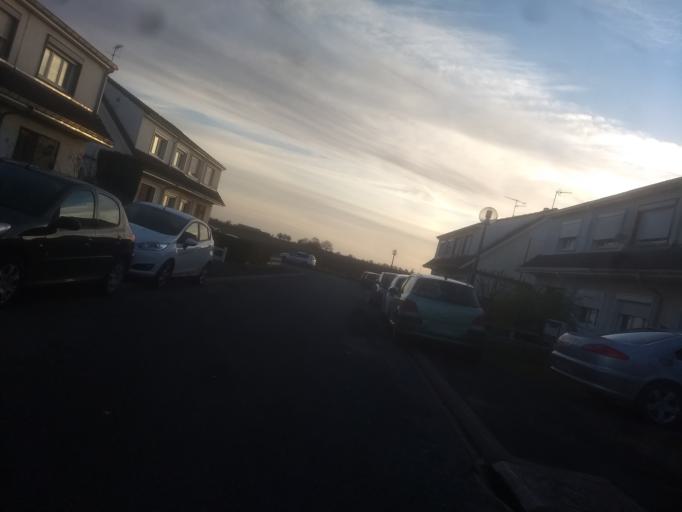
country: FR
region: Nord-Pas-de-Calais
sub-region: Departement du Pas-de-Calais
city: Agny
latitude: 50.2652
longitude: 2.7730
